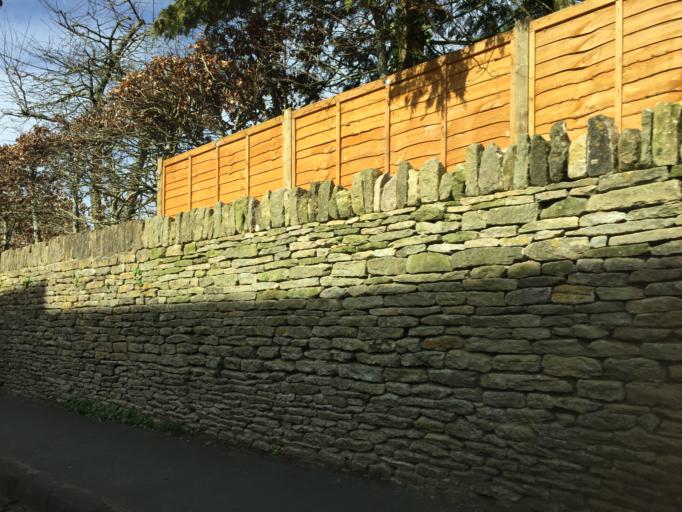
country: GB
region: England
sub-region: Wiltshire
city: Chippenham
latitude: 51.4967
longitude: -2.1413
